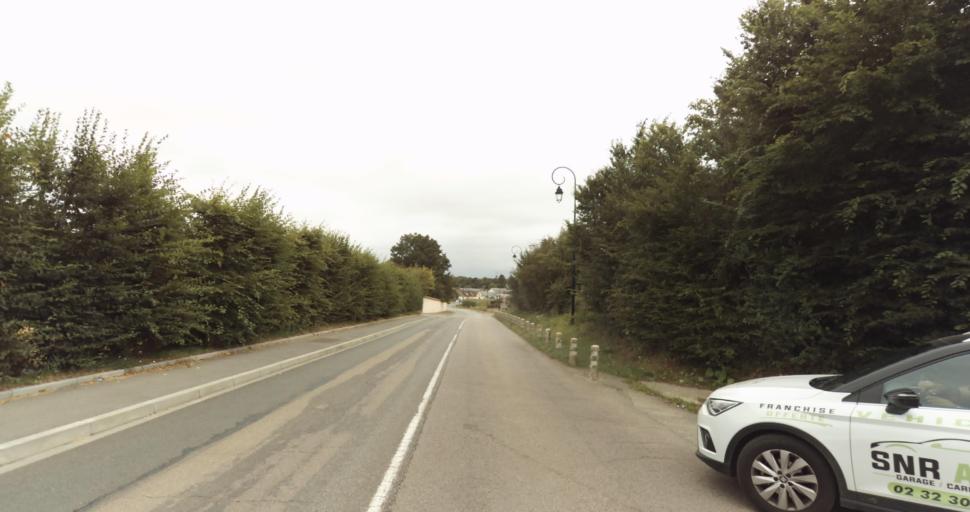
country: FR
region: Haute-Normandie
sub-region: Departement de l'Eure
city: Gravigny
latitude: 49.0300
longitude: 1.1916
